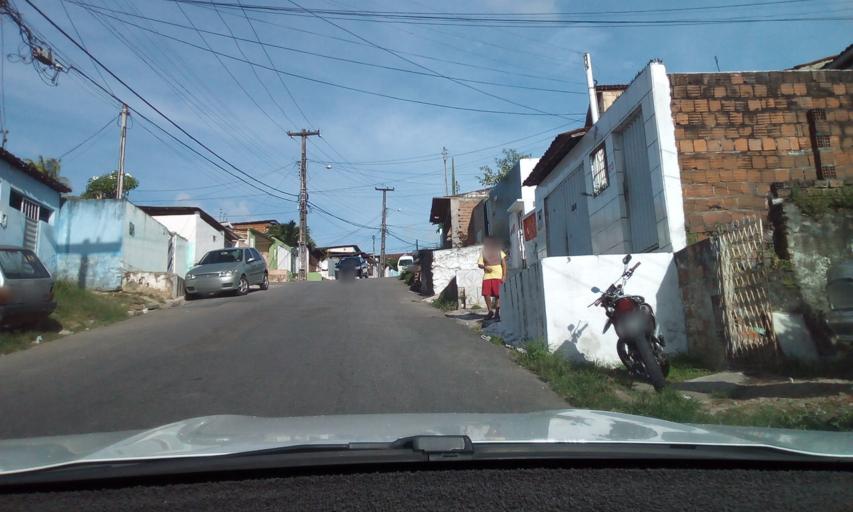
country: BR
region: Paraiba
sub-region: Joao Pessoa
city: Joao Pessoa
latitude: -7.1348
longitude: -34.8870
